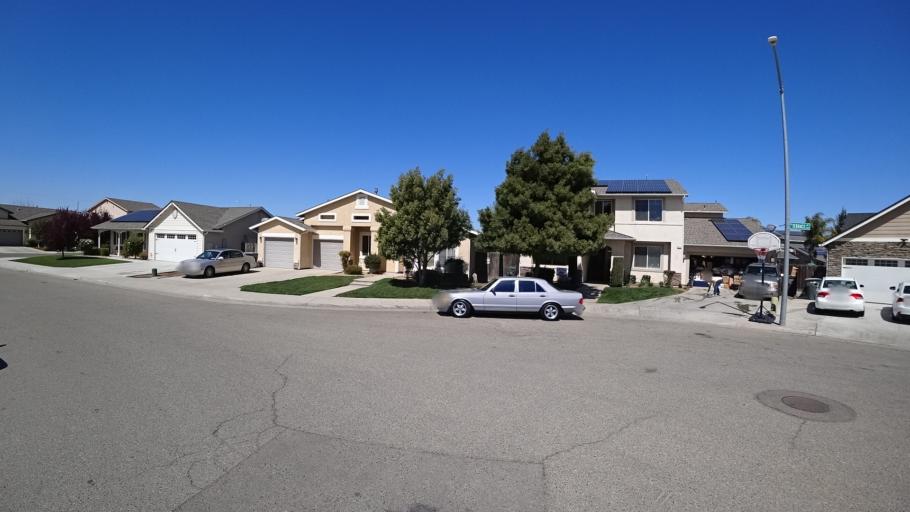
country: US
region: California
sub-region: Fresno County
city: West Park
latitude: 36.7728
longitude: -119.8881
